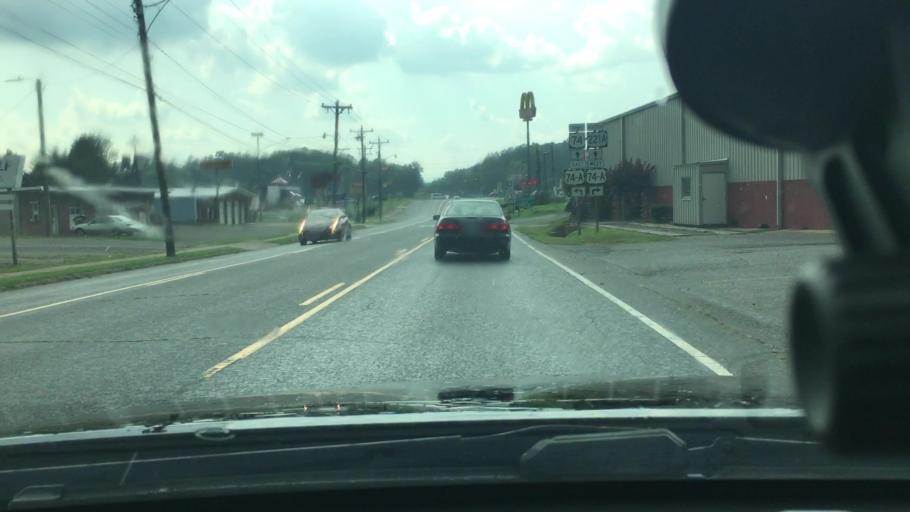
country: US
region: North Carolina
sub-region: Rutherford County
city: Spindale
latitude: 35.3617
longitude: -81.9392
